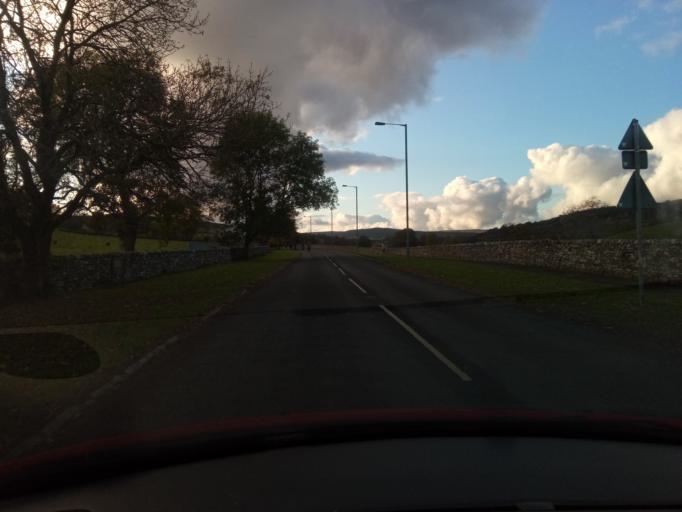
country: GB
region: England
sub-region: County Durham
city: Newbiggin
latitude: 54.7359
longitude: -2.1688
